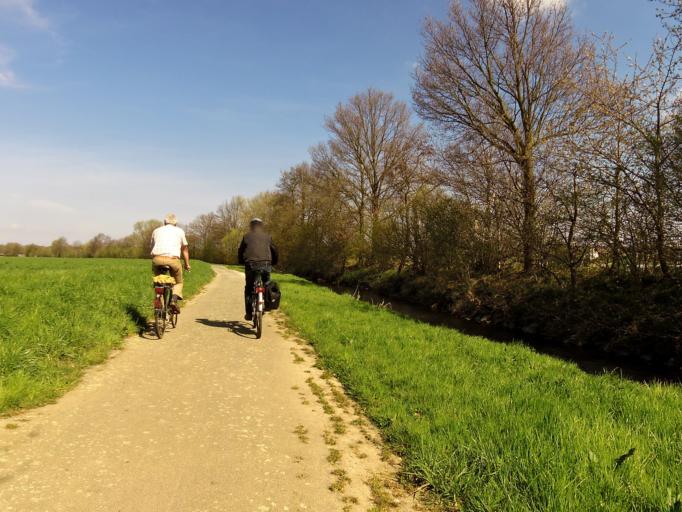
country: DE
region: North Rhine-Westphalia
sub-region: Regierungsbezirk Koln
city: Rheinbach
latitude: 50.6942
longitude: 6.9279
